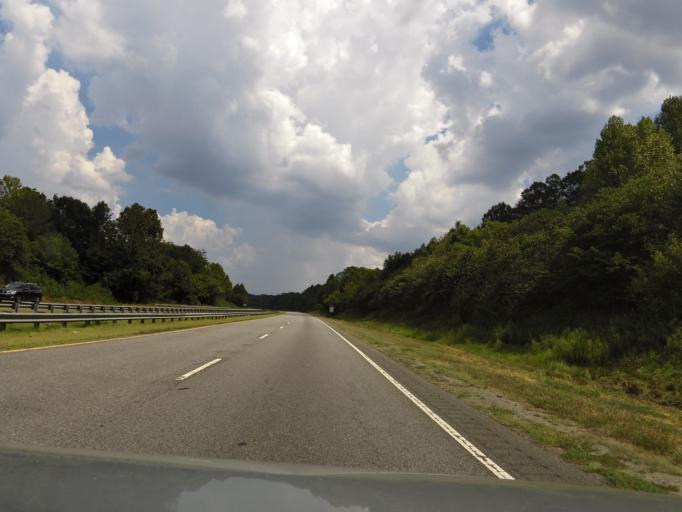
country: US
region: North Carolina
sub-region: Rutherford County
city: Rutherfordton
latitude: 35.2923
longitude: -81.9886
